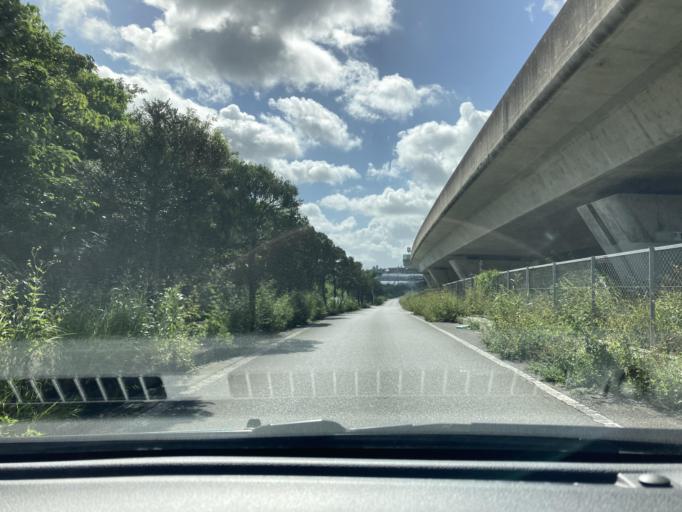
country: JP
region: Okinawa
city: Tomigusuku
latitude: 26.1817
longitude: 127.7317
